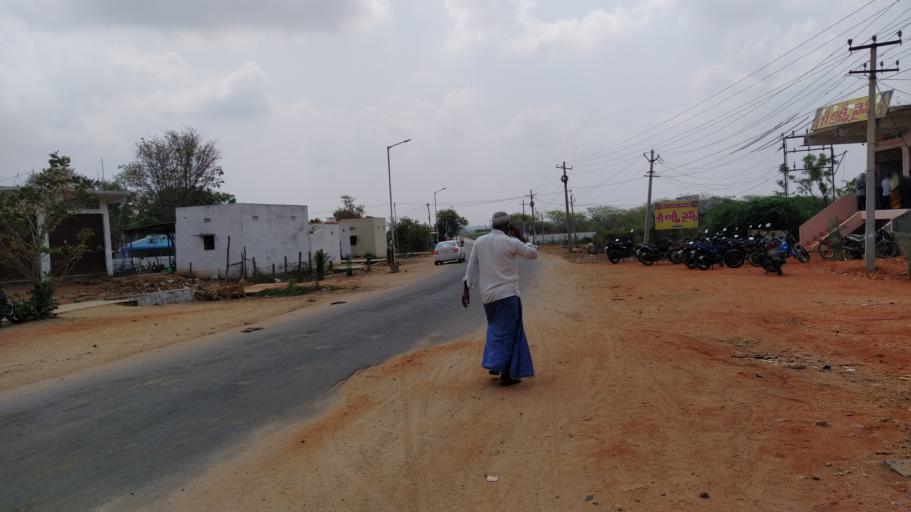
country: IN
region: Telangana
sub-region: Mahbubnagar
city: Nagar Karnul
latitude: 16.5186
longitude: 78.3597
